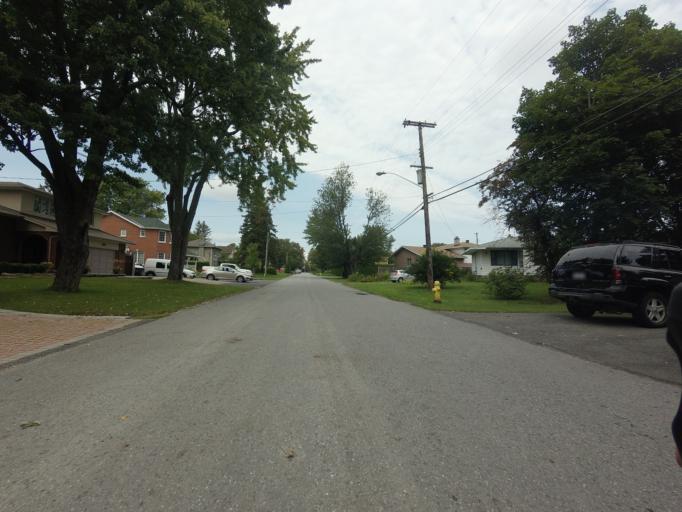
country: CA
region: Ontario
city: Ottawa
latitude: 45.3571
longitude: -75.7059
